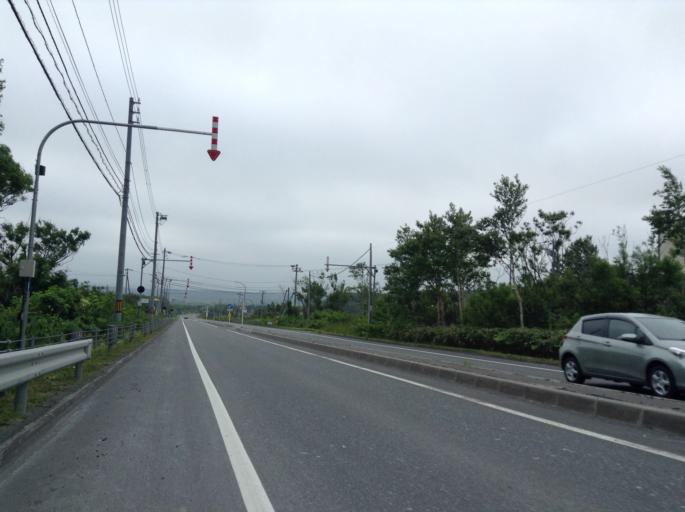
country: JP
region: Hokkaido
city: Wakkanai
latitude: 45.3725
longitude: 141.7190
